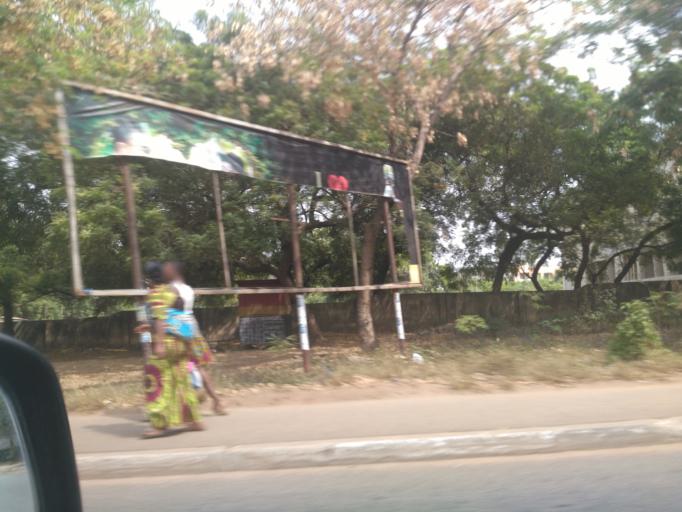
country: GH
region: Greater Accra
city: Accra
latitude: 5.5934
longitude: -0.1853
